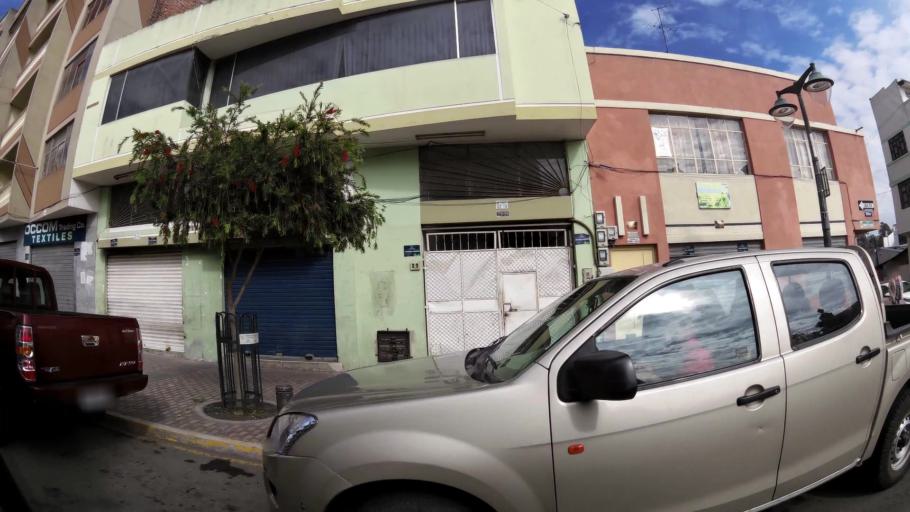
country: EC
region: Tungurahua
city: Ambato
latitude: -1.2535
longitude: -78.6452
